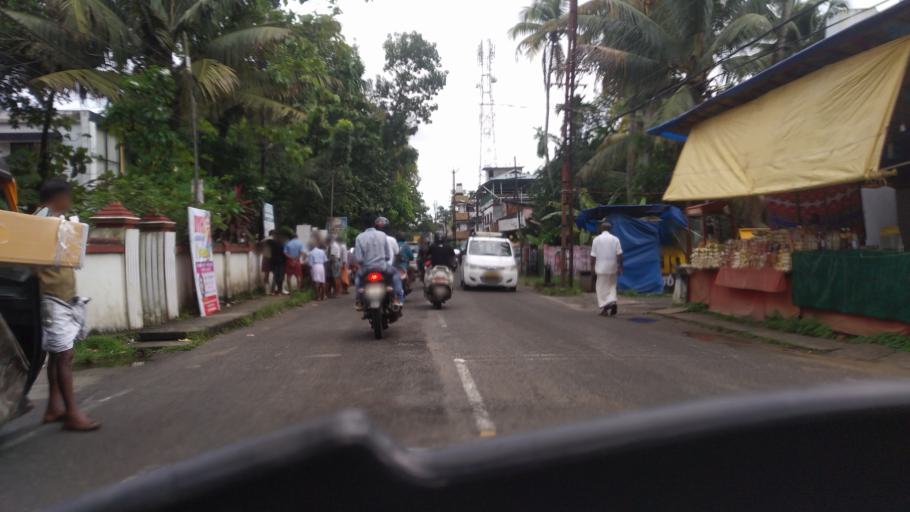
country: IN
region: Kerala
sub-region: Ernakulam
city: Elur
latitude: 10.0827
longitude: 76.2097
